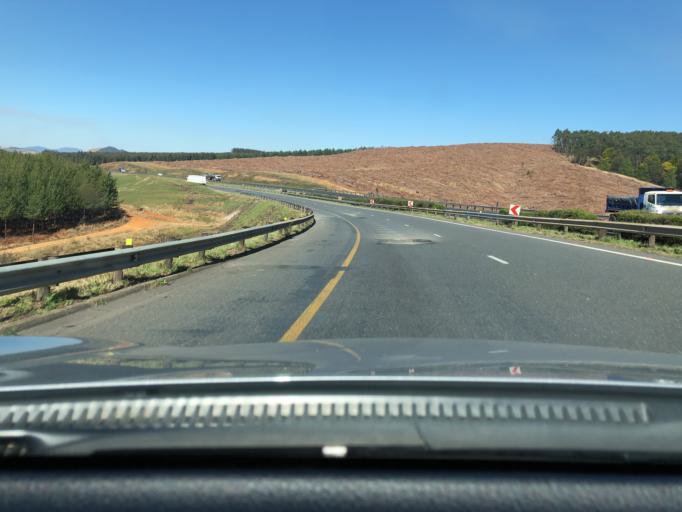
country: ZA
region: KwaZulu-Natal
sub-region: uMgungundlovu District Municipality
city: Howick
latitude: -29.3771
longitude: 30.1264
